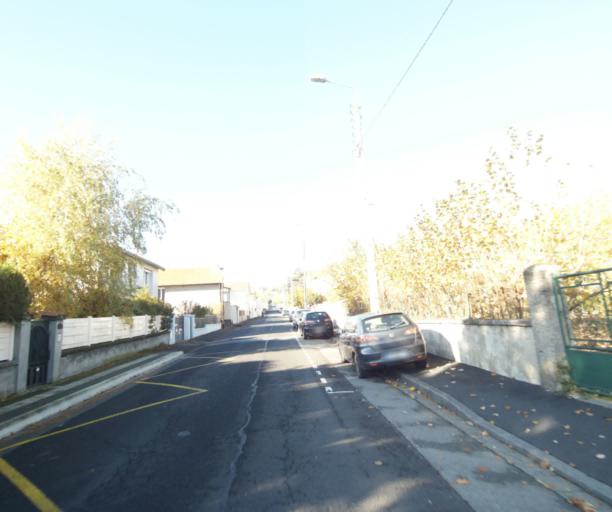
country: FR
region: Auvergne
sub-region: Departement du Puy-de-Dome
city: Clermont-Ferrand
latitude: 45.7947
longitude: 3.0824
